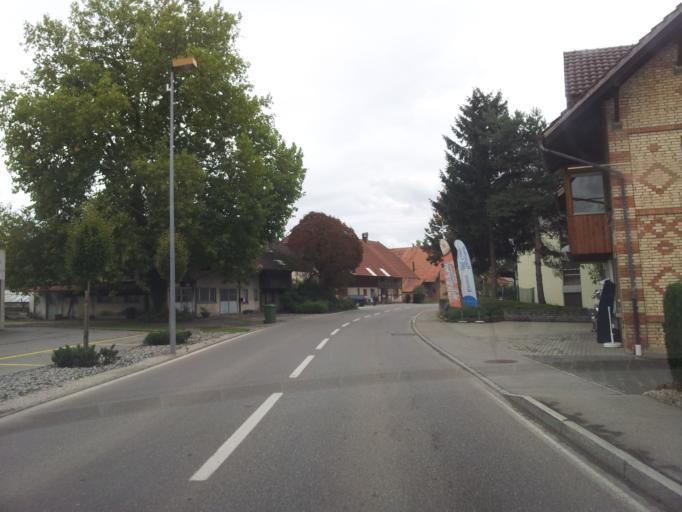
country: CH
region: Fribourg
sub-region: See District
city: Kerzers
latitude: 46.9806
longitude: 7.1988
